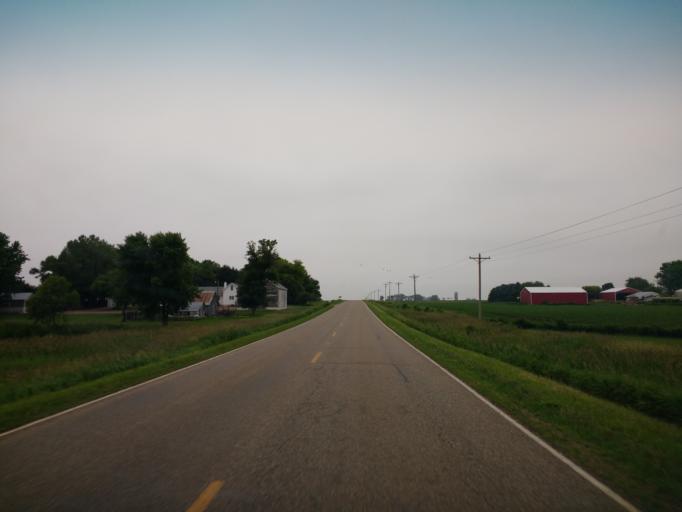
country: US
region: Iowa
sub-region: Sioux County
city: Alton
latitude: 43.0233
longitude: -95.8995
